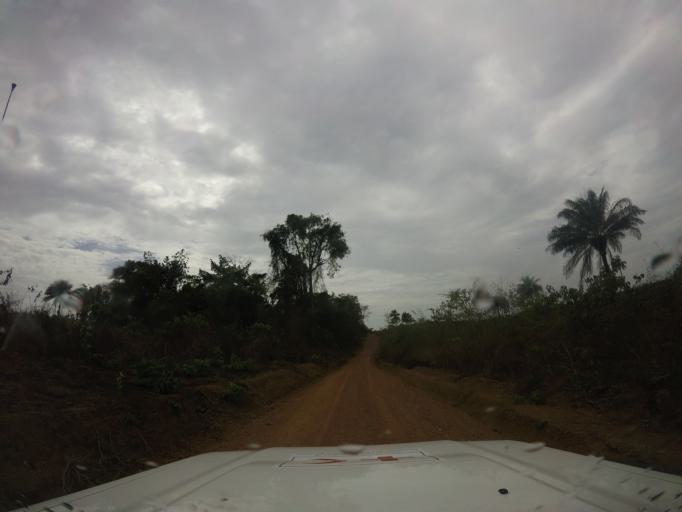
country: SL
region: Southern Province
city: Zimmi
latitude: 7.2208
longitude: -11.1835
